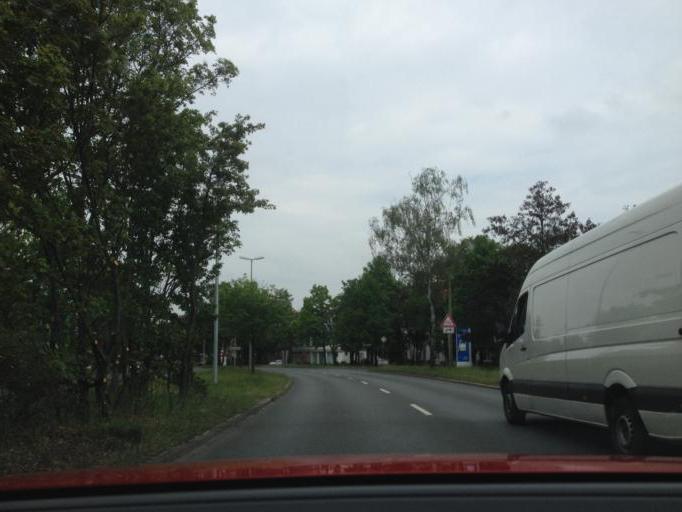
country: DE
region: Bavaria
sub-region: Regierungsbezirk Mittelfranken
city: Grossreuth bei Schweinau
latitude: 49.4351
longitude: 11.0384
